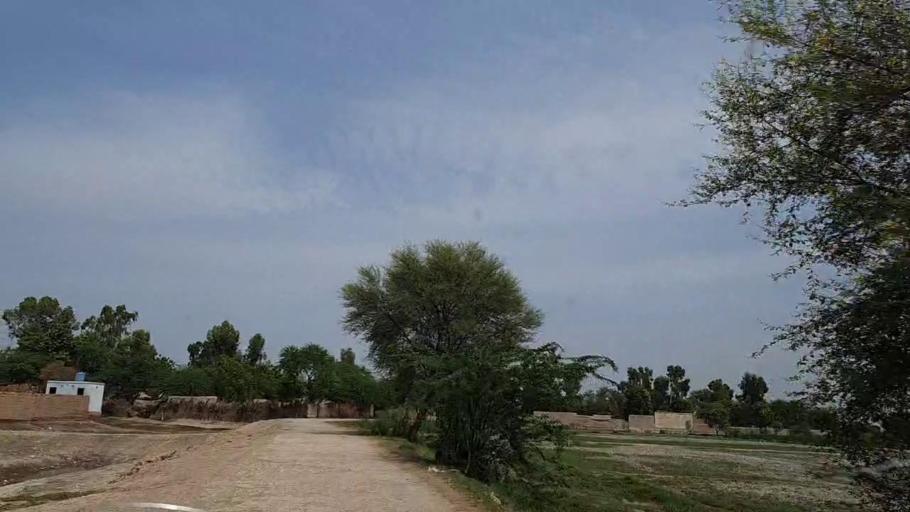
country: PK
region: Sindh
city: Khanpur
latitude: 27.8576
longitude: 69.4243
